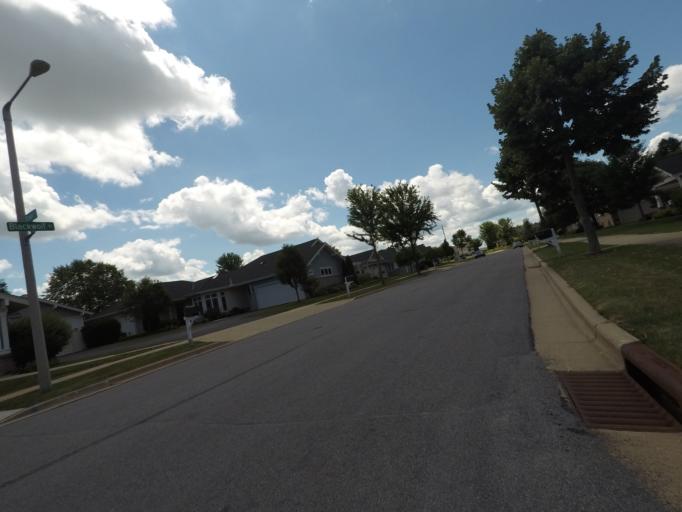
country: US
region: Wisconsin
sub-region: Dane County
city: Middleton
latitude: 43.0721
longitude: -89.5346
